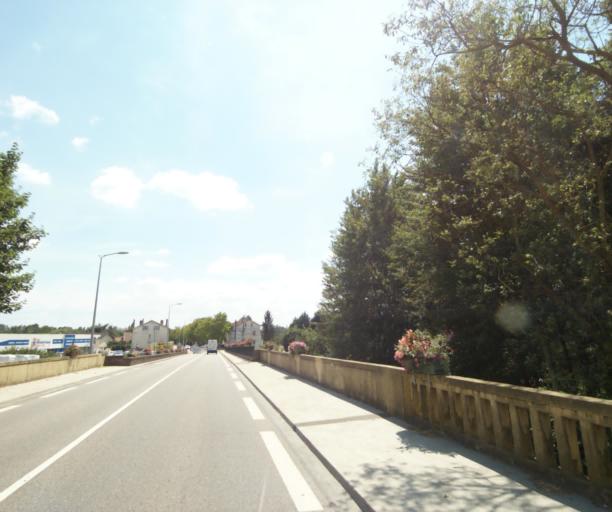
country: FR
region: Lorraine
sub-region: Departement de Meurthe-et-Moselle
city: Luneville
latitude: 48.5826
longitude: 6.4812
